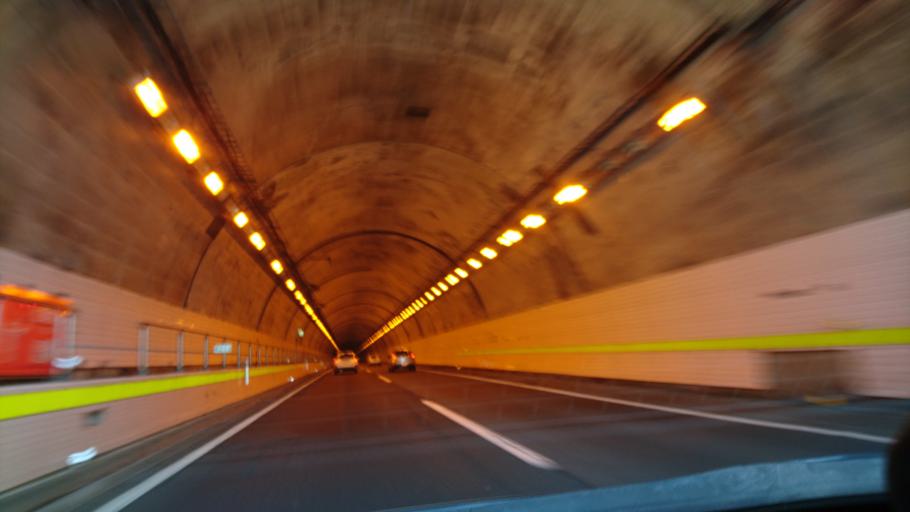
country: JP
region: Iwate
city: Ichinoseki
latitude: 38.9475
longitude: 141.1049
